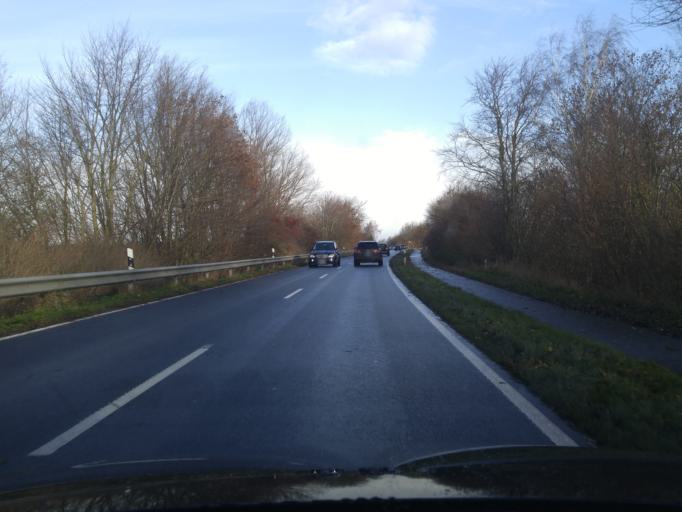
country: DE
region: Schleswig-Holstein
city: Timmendorfer Strand
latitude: 53.9812
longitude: 10.7723
